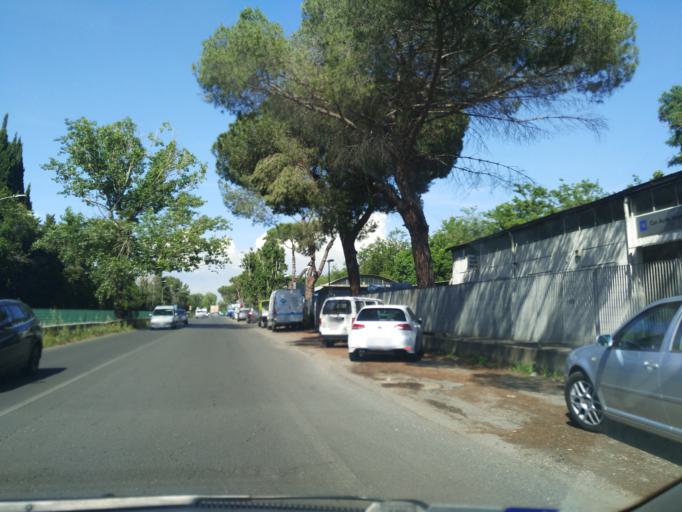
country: IT
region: Latium
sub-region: Citta metropolitana di Roma Capitale
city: Vitinia
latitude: 41.8212
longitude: 12.4384
